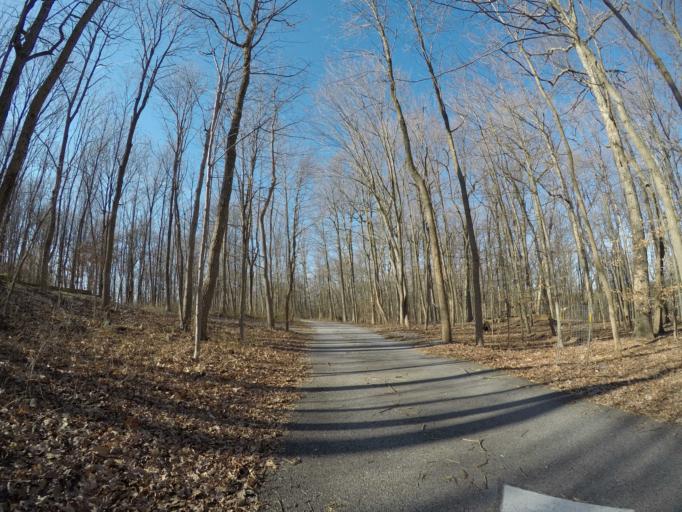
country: US
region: Maryland
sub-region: Howard County
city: Ellicott City
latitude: 39.2870
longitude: -76.7877
